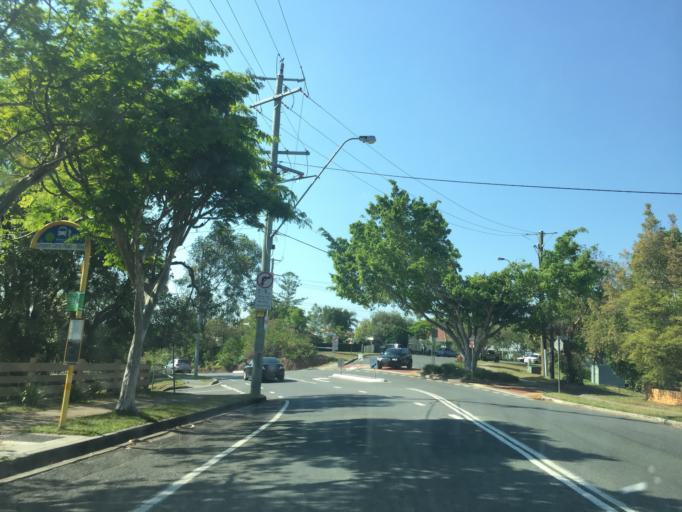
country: AU
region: Queensland
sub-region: Brisbane
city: Milton
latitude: -27.4500
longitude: 152.9774
